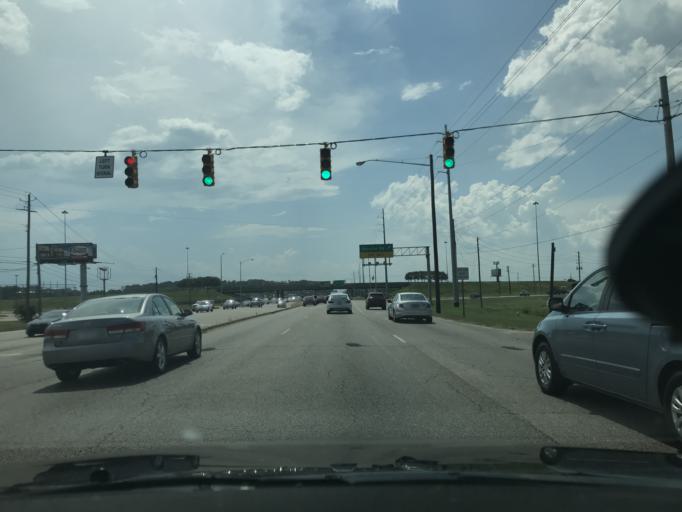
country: US
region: Alabama
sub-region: Montgomery County
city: Montgomery
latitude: 32.3821
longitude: -86.2068
